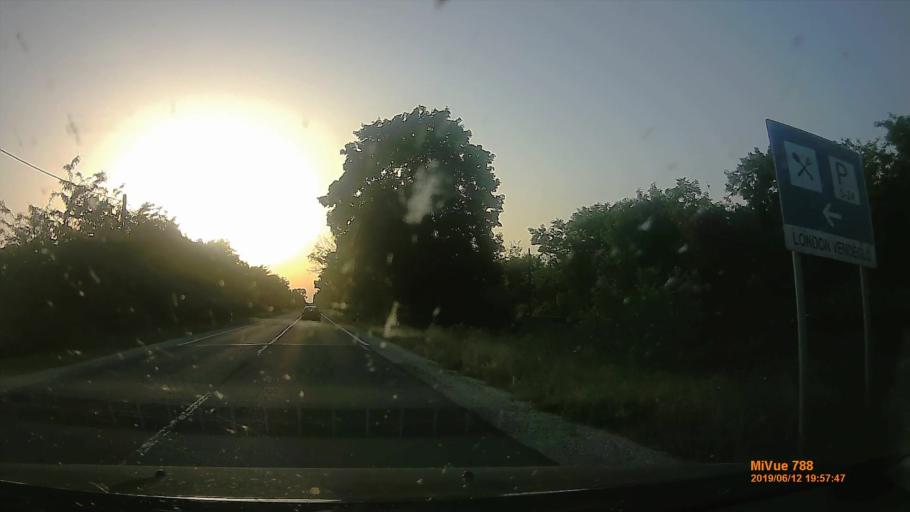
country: HU
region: Pest
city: Dabas
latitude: 47.1763
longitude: 19.3588
